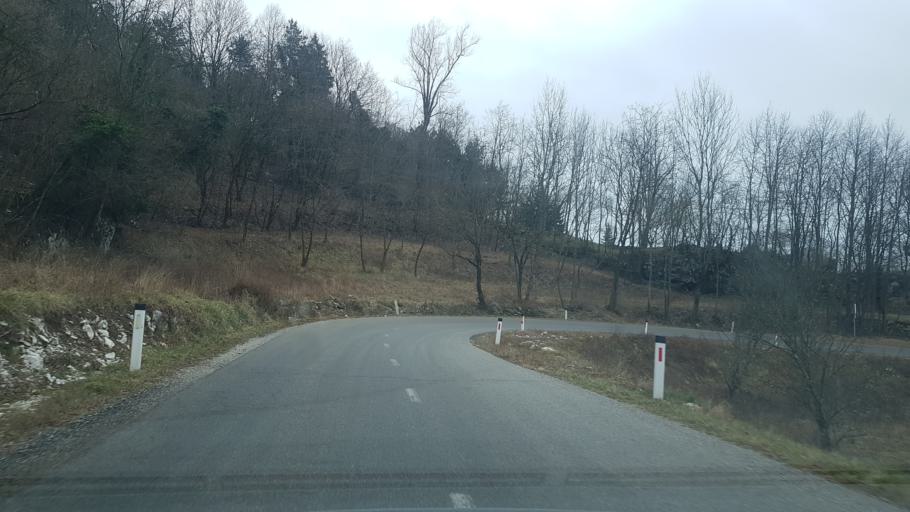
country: SI
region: Kanal
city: Deskle
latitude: 46.0342
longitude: 13.6690
